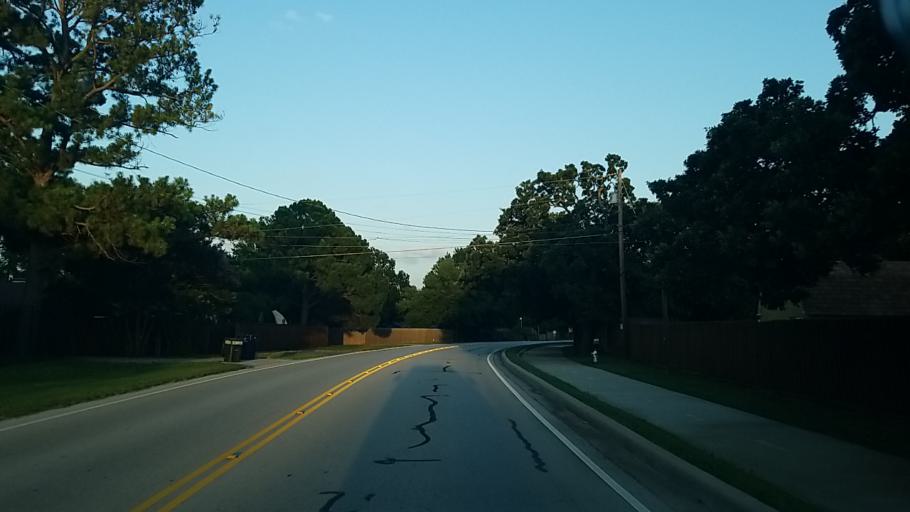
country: US
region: Texas
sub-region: Denton County
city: Highland Village
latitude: 33.0920
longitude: -97.0370
